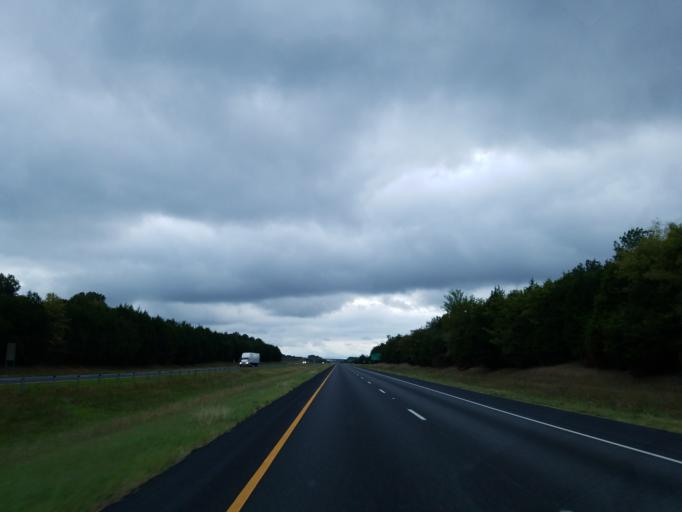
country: US
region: Alabama
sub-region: Sumter County
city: Livingston
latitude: 32.7078
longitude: -88.1356
